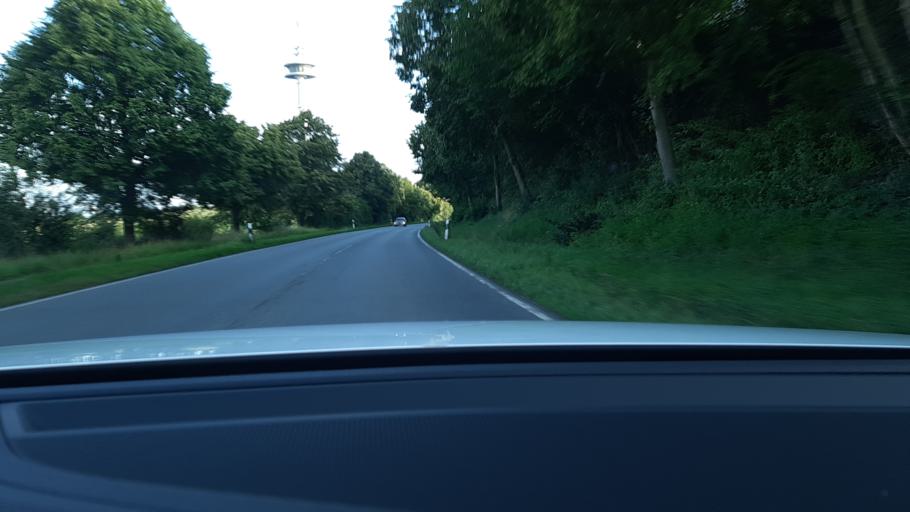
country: DE
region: Schleswig-Holstein
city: Stockelsdorf
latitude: 53.9120
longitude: 10.6405
